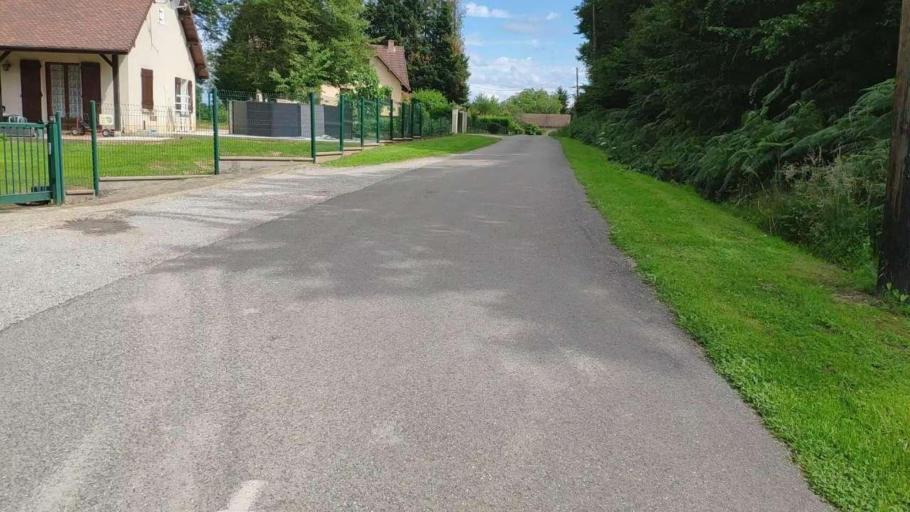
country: FR
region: Franche-Comte
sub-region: Departement du Jura
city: Bletterans
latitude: 46.7988
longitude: 5.4504
